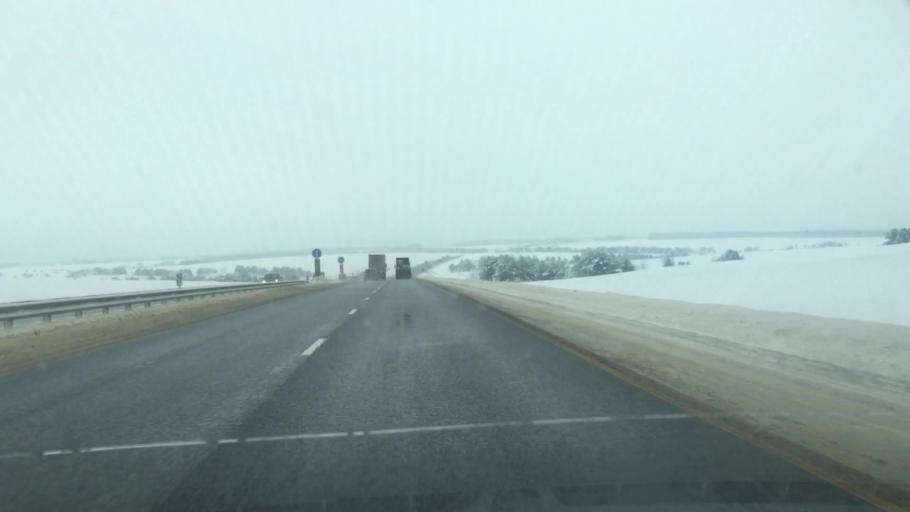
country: RU
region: Lipetsk
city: Stanovoye
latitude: 52.7922
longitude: 38.3479
